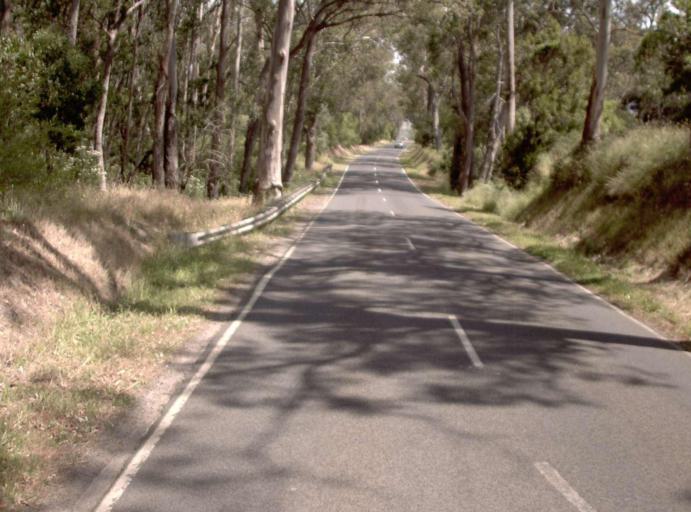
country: AU
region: Victoria
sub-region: Latrobe
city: Traralgon
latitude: -38.2913
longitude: 146.5394
